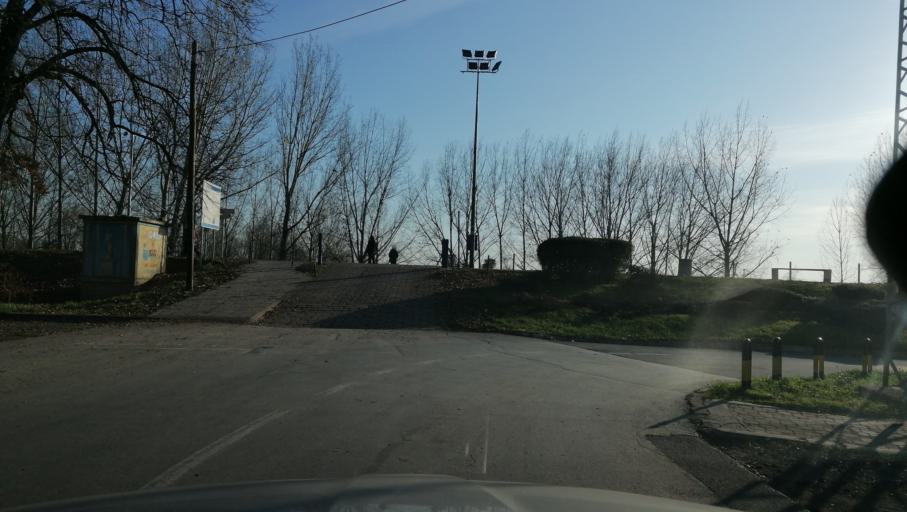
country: RS
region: Autonomna Pokrajina Vojvodina
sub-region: Sremski Okrug
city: Sremska Mitrovica
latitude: 44.9627
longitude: 19.6132
